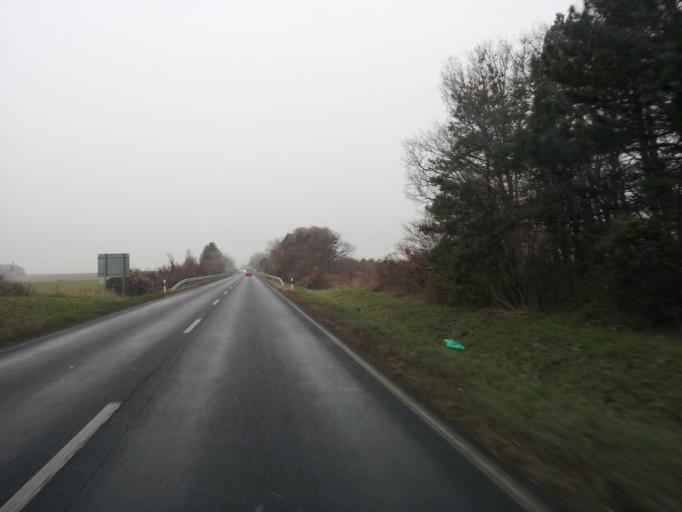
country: HU
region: Veszprem
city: Ajka
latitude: 47.1423
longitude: 17.6066
